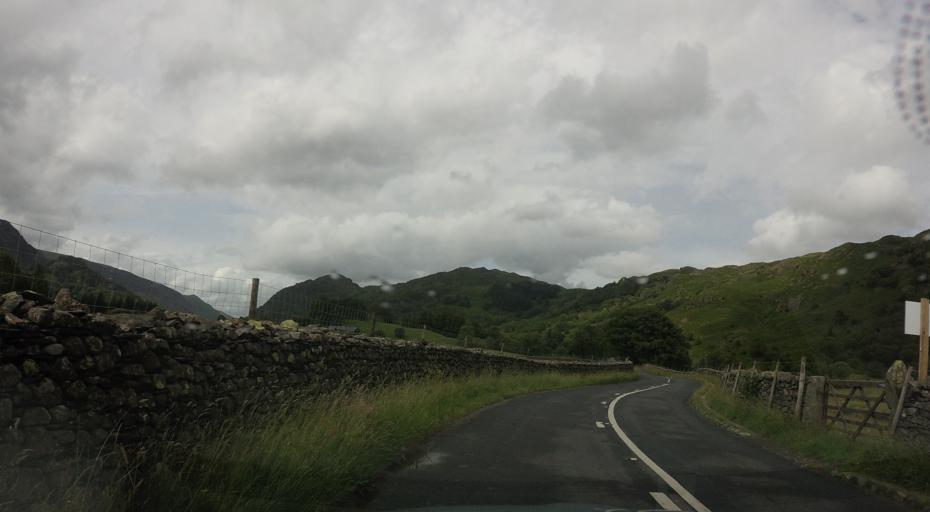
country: GB
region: England
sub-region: Cumbria
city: Keswick
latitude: 54.5179
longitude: -3.1488
